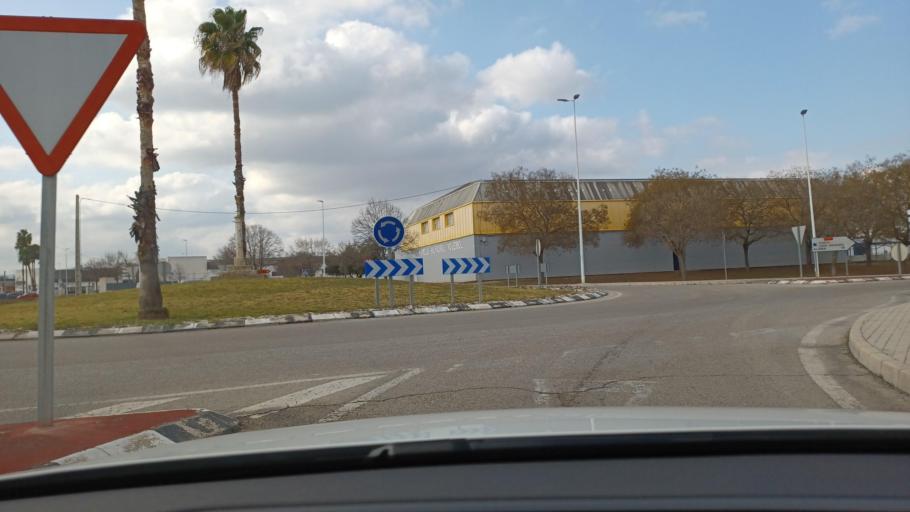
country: ES
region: Valencia
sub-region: Provincia de Valencia
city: Xativa
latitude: 38.9954
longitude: -0.5130
